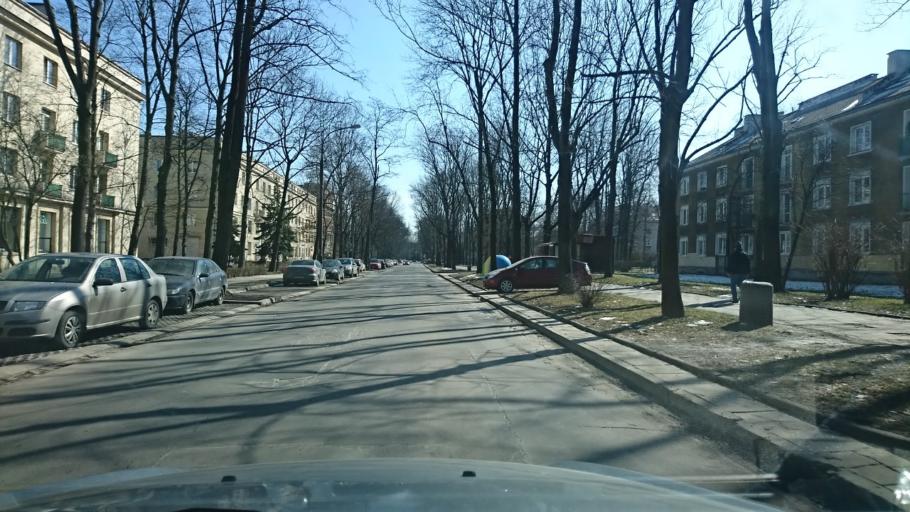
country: PL
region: Lesser Poland Voivodeship
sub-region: Powiat wielicki
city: Kokotow
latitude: 50.0735
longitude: 20.0488
